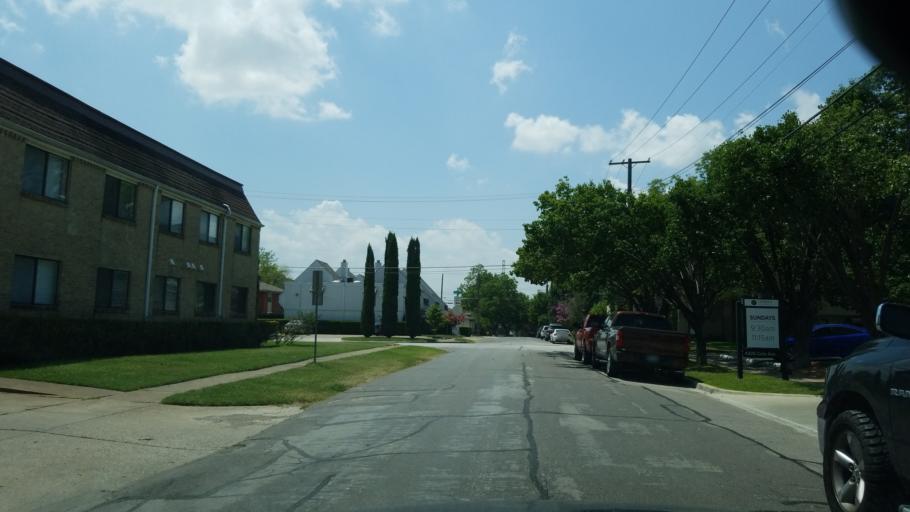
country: US
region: Texas
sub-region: Dallas County
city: Highland Park
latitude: 32.8181
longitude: -96.7911
